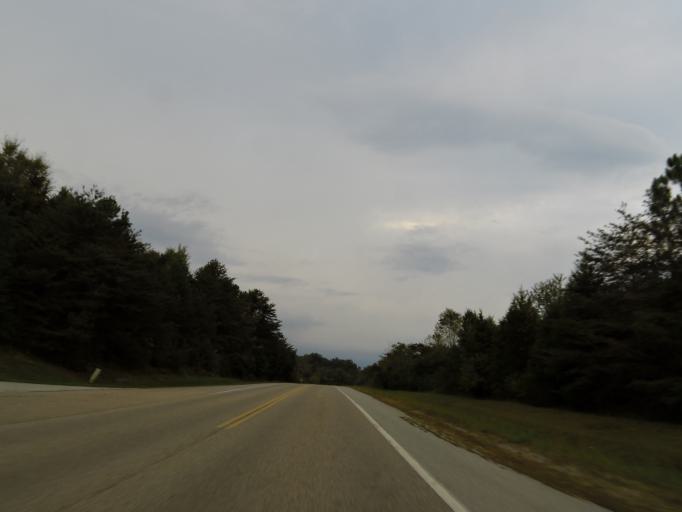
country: US
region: Tennessee
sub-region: Loudon County
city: Loudon
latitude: 35.6657
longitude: -84.2814
